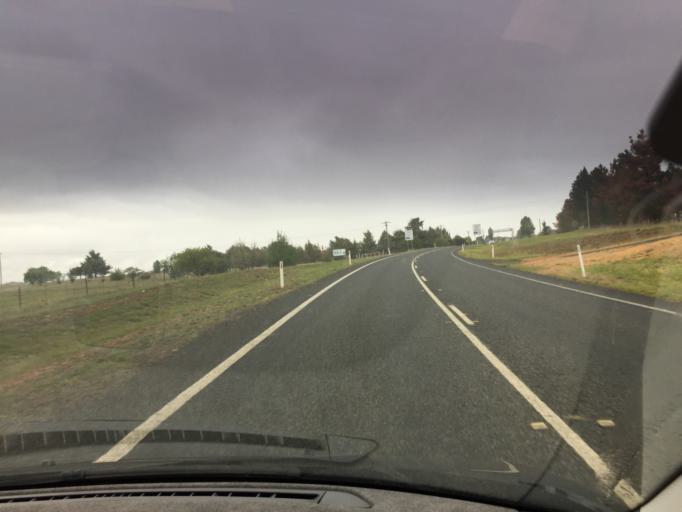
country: AU
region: New South Wales
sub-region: Cooma-Monaro
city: Cooma
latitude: -36.2083
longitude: 149.1569
